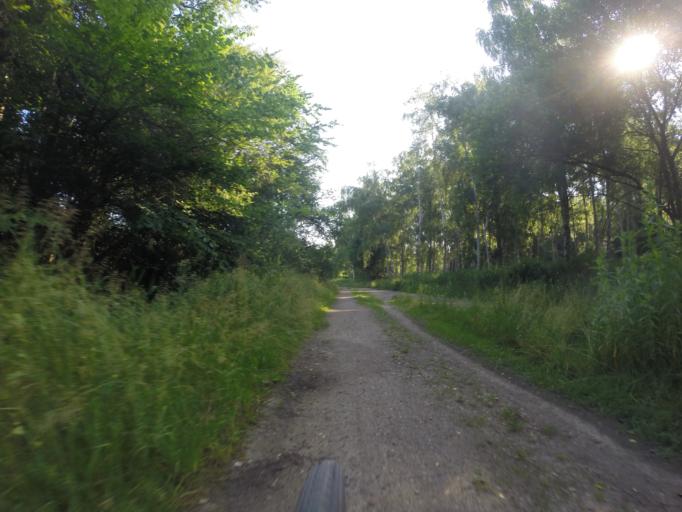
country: DK
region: Capital Region
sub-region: Ballerup Kommune
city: Ballerup
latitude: 55.7010
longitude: 12.3360
